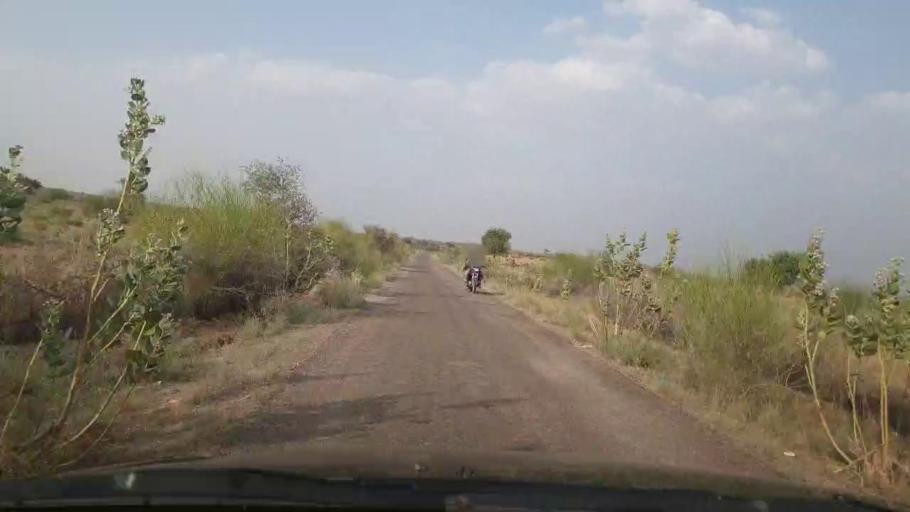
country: PK
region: Sindh
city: Islamkot
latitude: 25.0622
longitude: 70.5624
